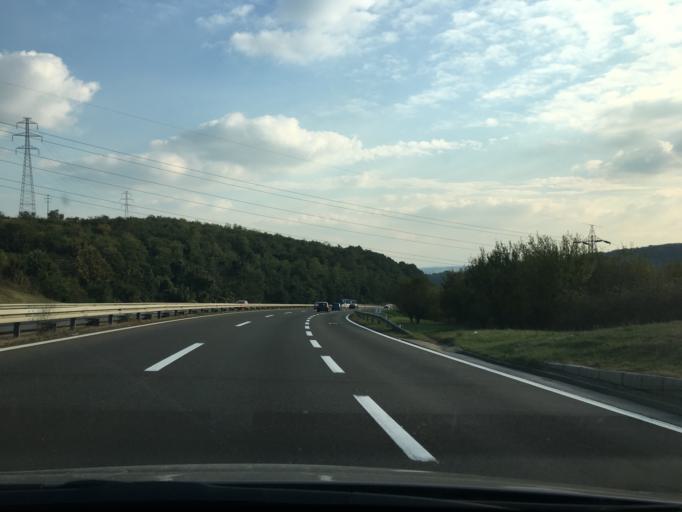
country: RS
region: Central Serbia
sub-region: Belgrade
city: Zvezdara
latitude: 44.7528
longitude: 20.5399
